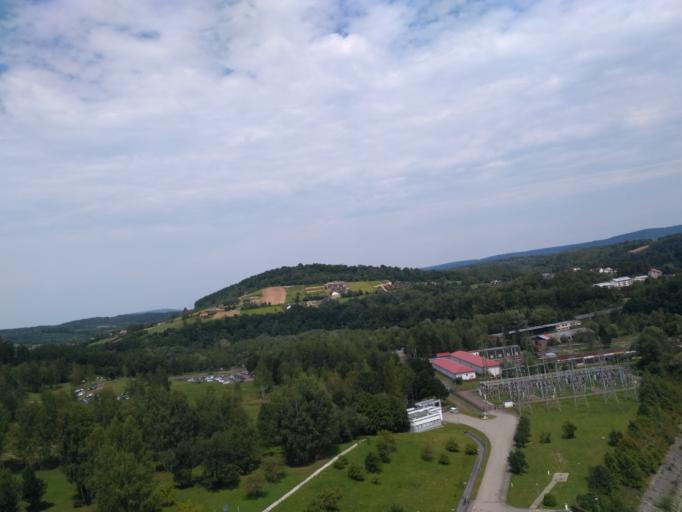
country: PL
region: Subcarpathian Voivodeship
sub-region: Powiat leski
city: Polanczyk
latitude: 49.3955
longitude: 22.4535
